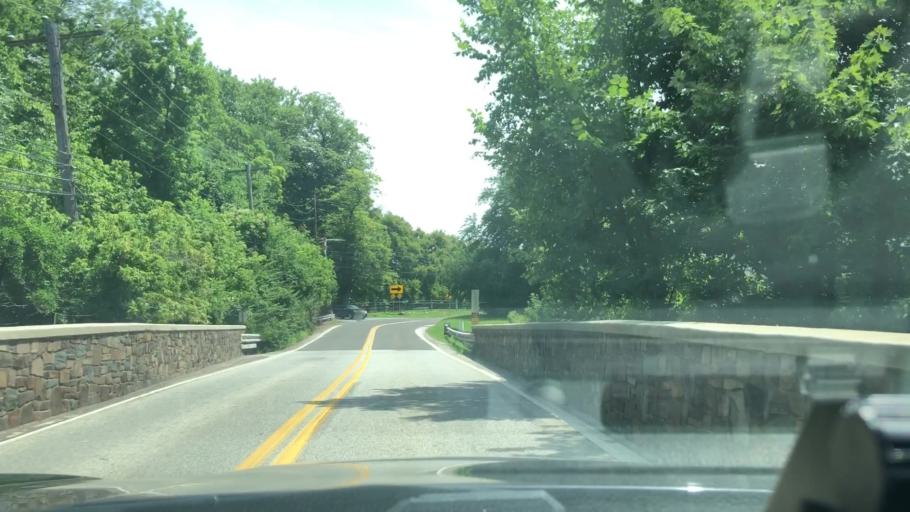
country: US
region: Pennsylvania
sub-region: Montgomery County
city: Flourtown
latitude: 40.1019
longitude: -75.2304
